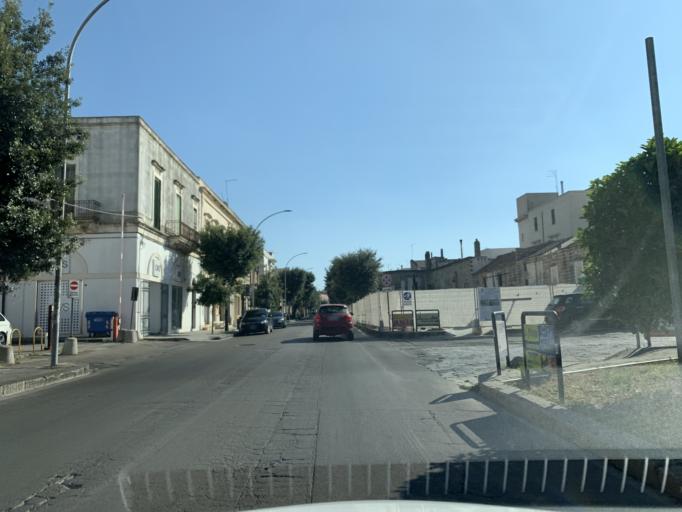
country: IT
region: Apulia
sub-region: Provincia di Lecce
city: Nardo
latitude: 40.1779
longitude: 18.0349
